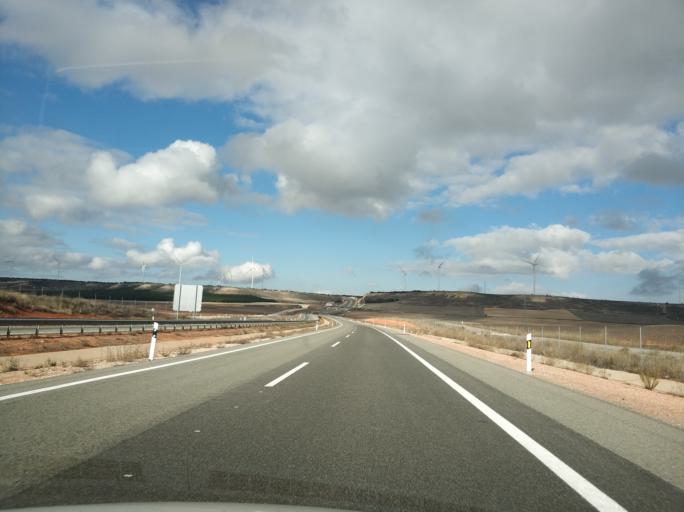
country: ES
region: Castille and Leon
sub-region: Provincia de Soria
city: Alcubilla de las Penas
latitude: 41.2751
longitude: -2.4747
